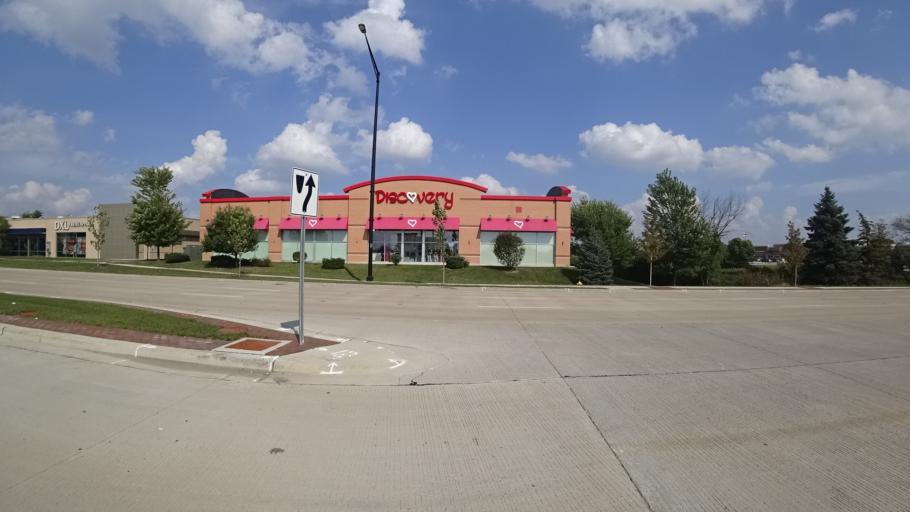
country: US
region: Illinois
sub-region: Cook County
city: Orland Hills
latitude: 41.6053
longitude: -87.8531
